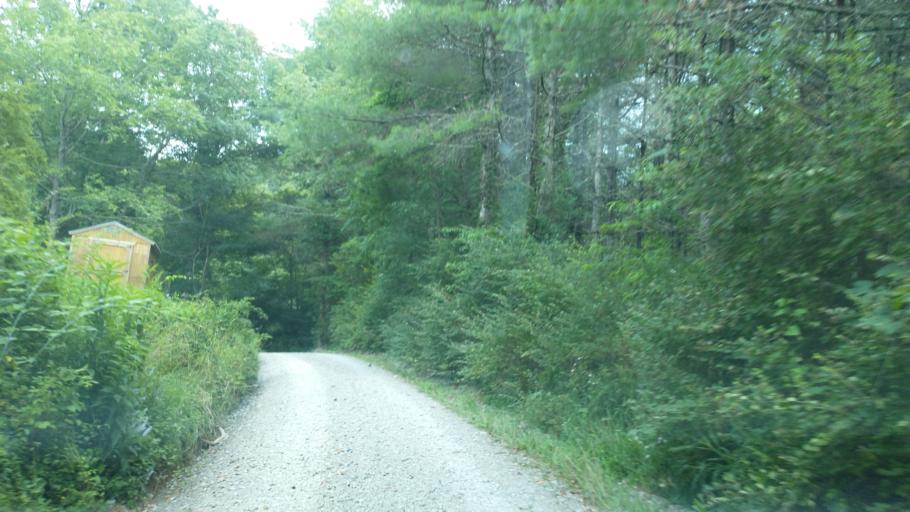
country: US
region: West Virginia
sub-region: Mercer County
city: Athens
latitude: 37.4364
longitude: -81.0037
